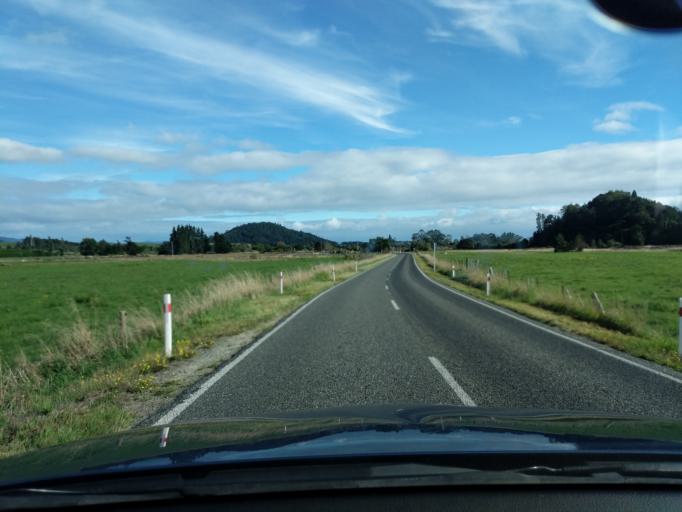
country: NZ
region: Tasman
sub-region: Tasman District
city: Takaka
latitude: -40.8487
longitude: 172.8399
